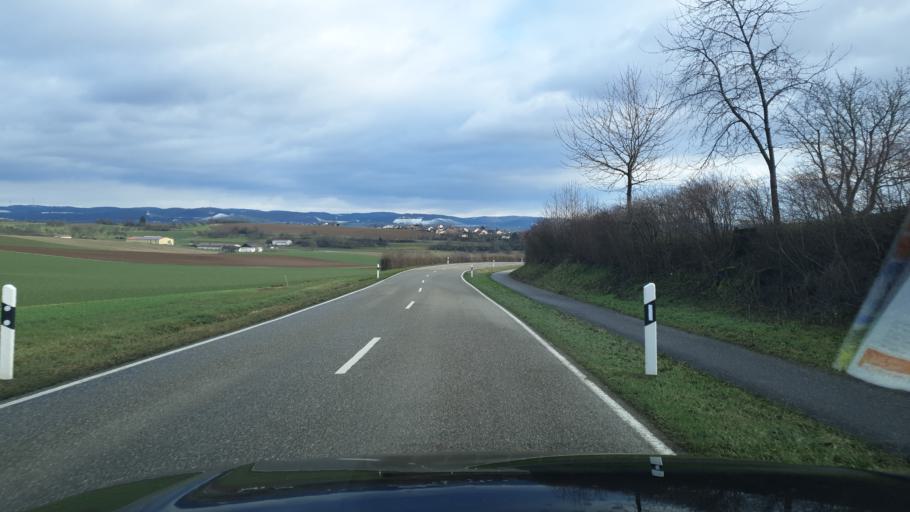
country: DE
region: Baden-Wuerttemberg
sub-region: Regierungsbezirk Stuttgart
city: Ilsfeld
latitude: 49.0625
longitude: 9.2274
